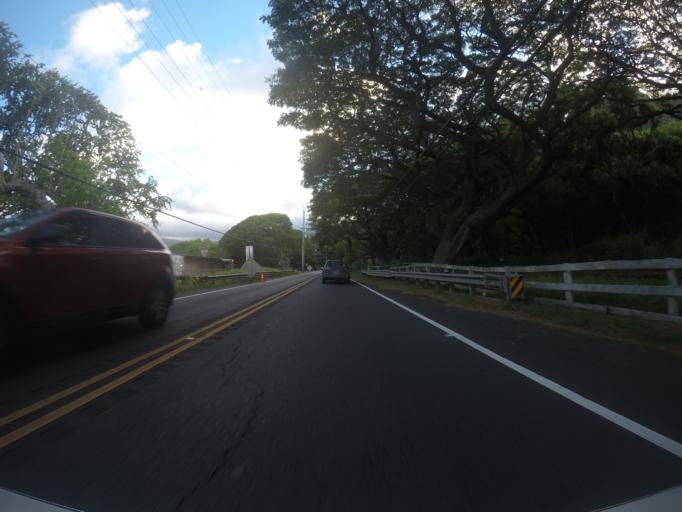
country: US
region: Hawaii
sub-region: Honolulu County
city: Ka'a'awa
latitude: 21.5165
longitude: -157.8395
